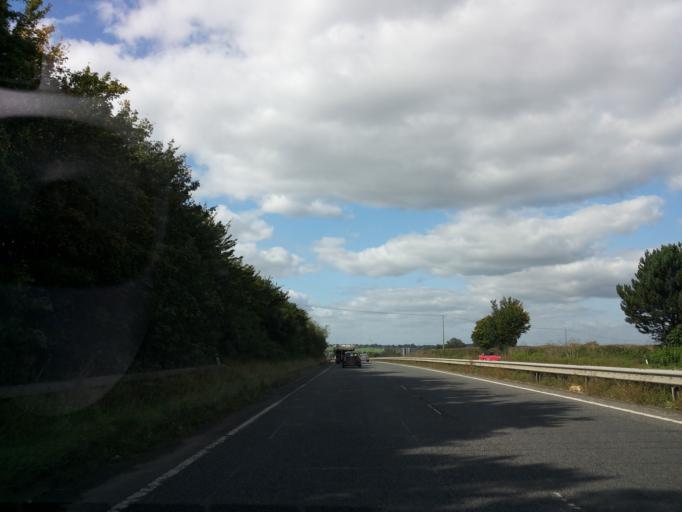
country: GB
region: England
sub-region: Wiltshire
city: Wingfield
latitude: 51.2678
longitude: -2.2808
